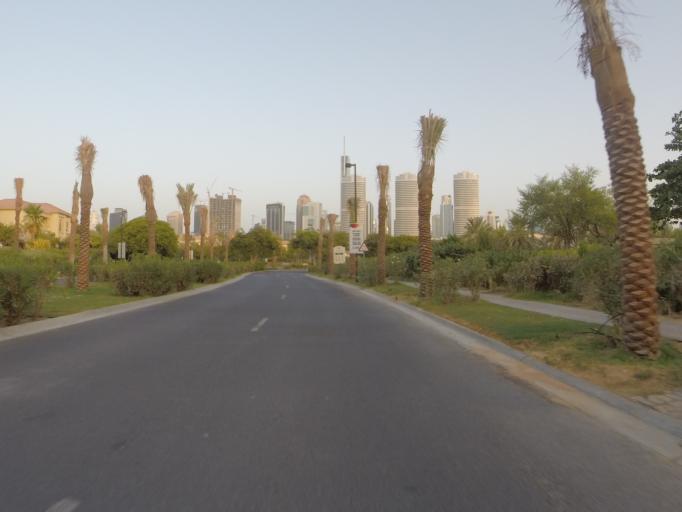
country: AE
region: Dubai
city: Dubai
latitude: 25.0635
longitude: 55.1525
